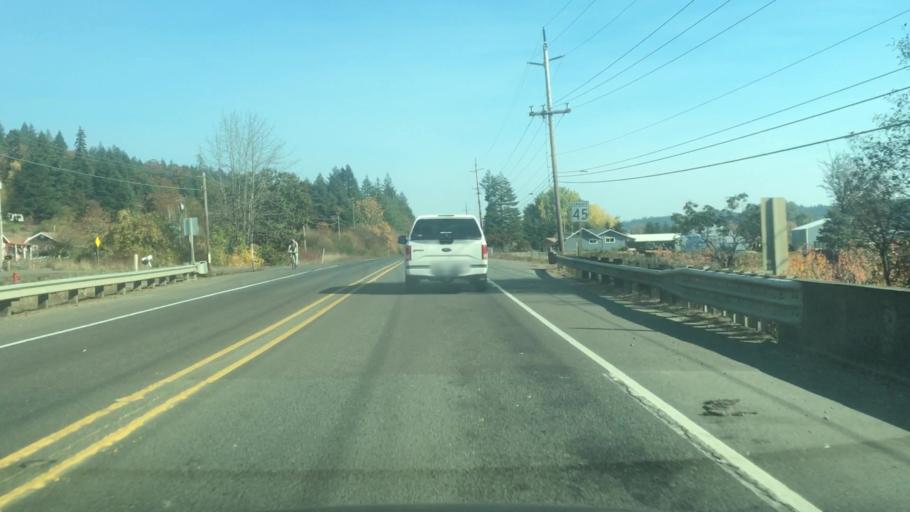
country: US
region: Oregon
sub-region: Polk County
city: Grand Ronde
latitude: 45.0582
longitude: -123.6019
